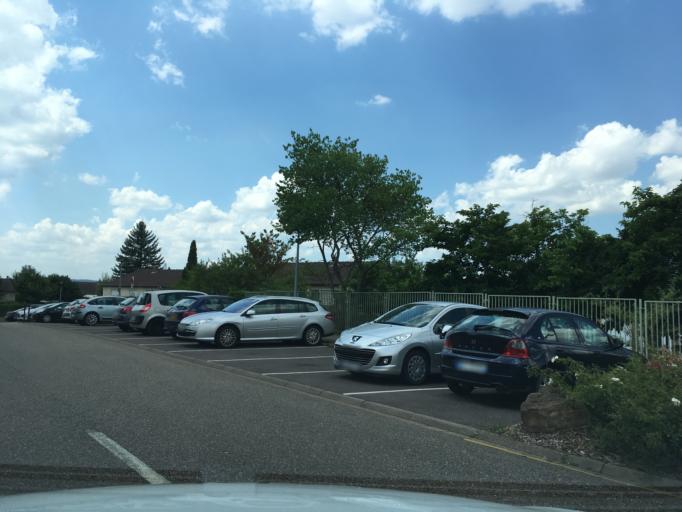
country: FR
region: Lorraine
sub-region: Departement de la Moselle
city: Saint-Julien-les-Metz
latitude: 49.1226
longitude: 6.2200
